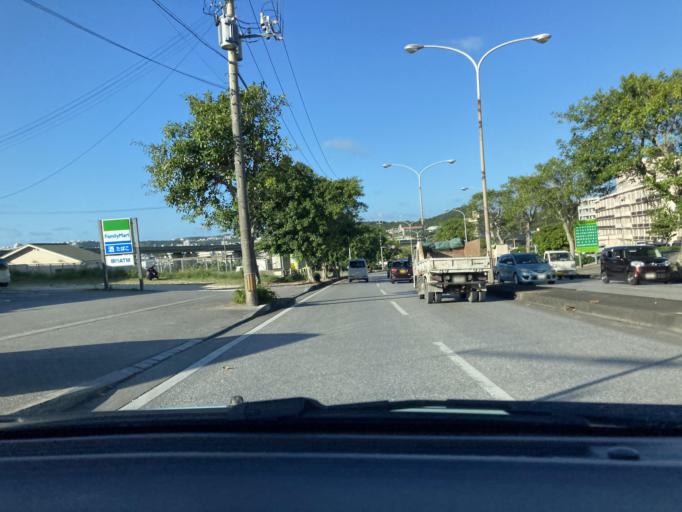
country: JP
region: Okinawa
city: Tomigusuku
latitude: 26.1766
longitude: 127.7132
